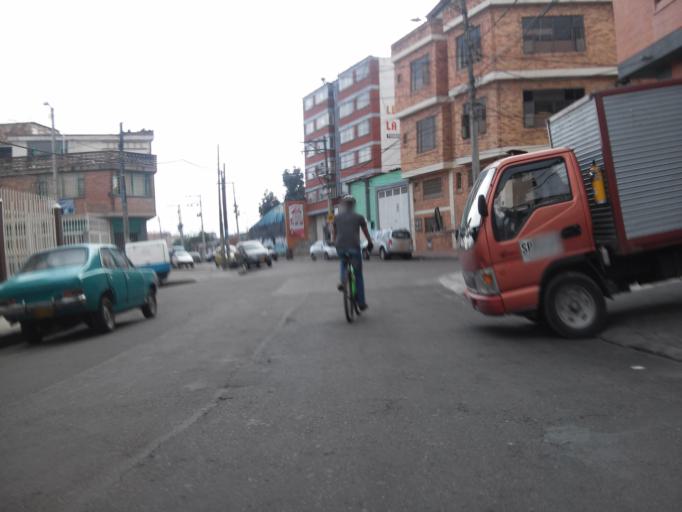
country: CO
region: Bogota D.C.
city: Bogota
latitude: 4.6185
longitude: -74.1433
